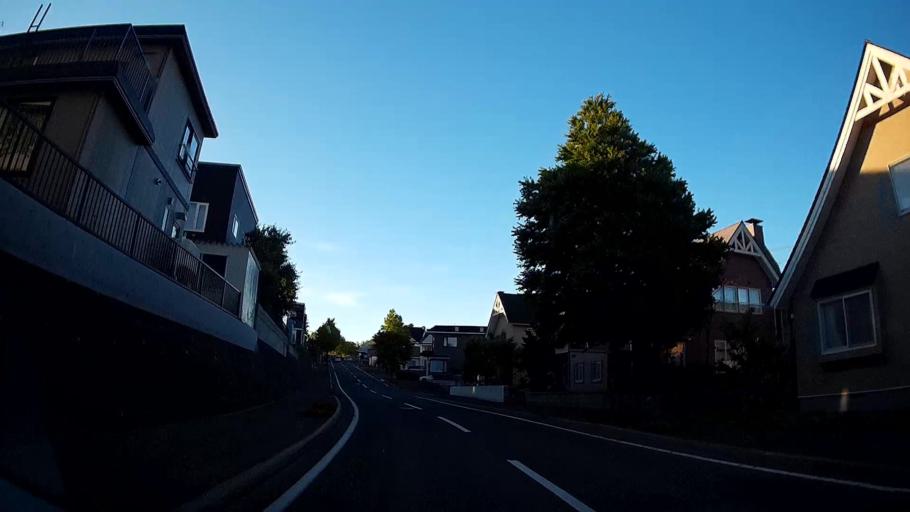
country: JP
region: Hokkaido
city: Otaru
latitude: 43.1634
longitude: 141.0415
